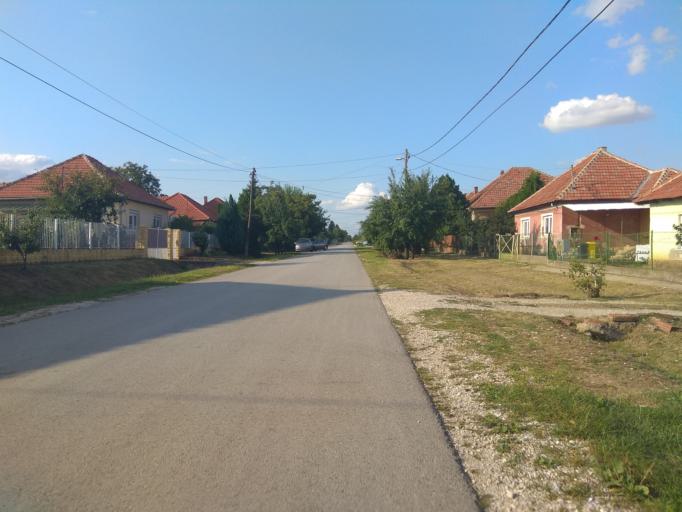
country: HU
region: Borsod-Abauj-Zemplen
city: Emod
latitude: 47.9319
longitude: 20.8077
